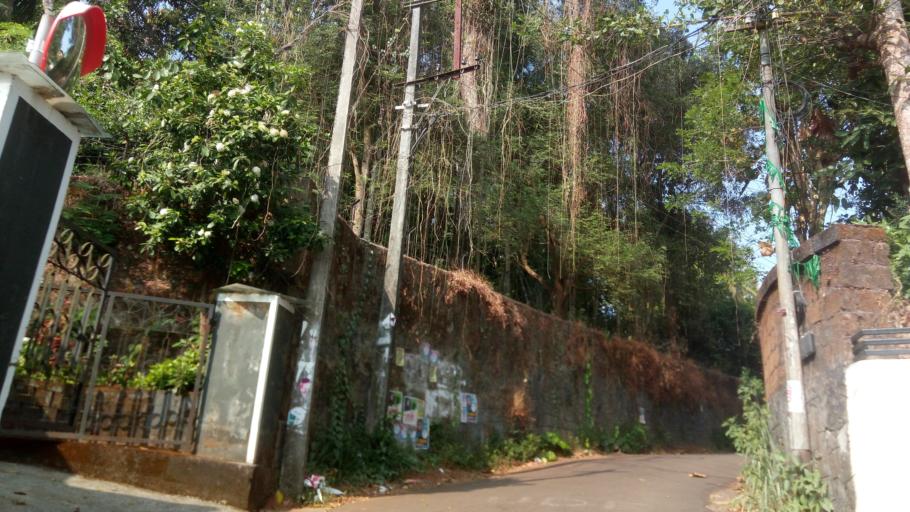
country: IN
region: Kerala
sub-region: Malappuram
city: Malappuram
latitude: 10.9987
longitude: 75.9996
